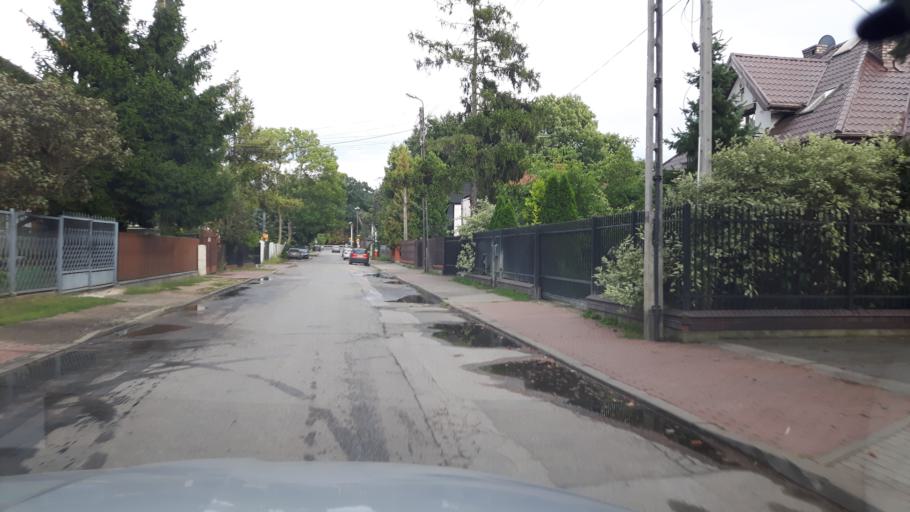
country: PL
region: Masovian Voivodeship
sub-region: Powiat wolominski
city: Marki
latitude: 52.3241
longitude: 21.1013
